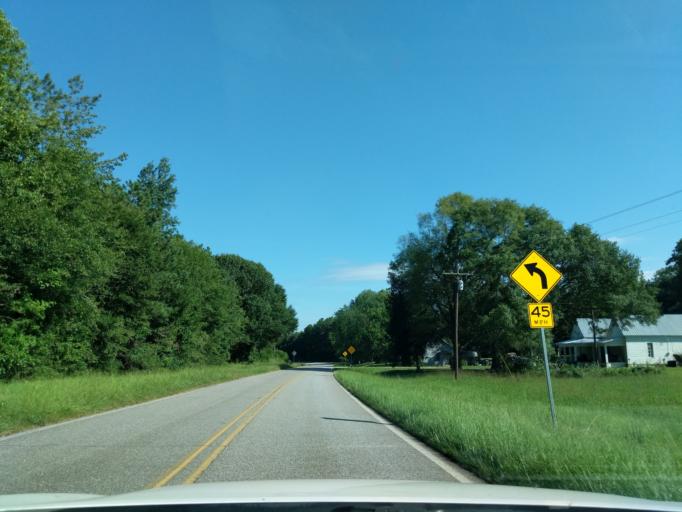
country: US
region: Georgia
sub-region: Oglethorpe County
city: Lexington
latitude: 33.9054
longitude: -83.0002
